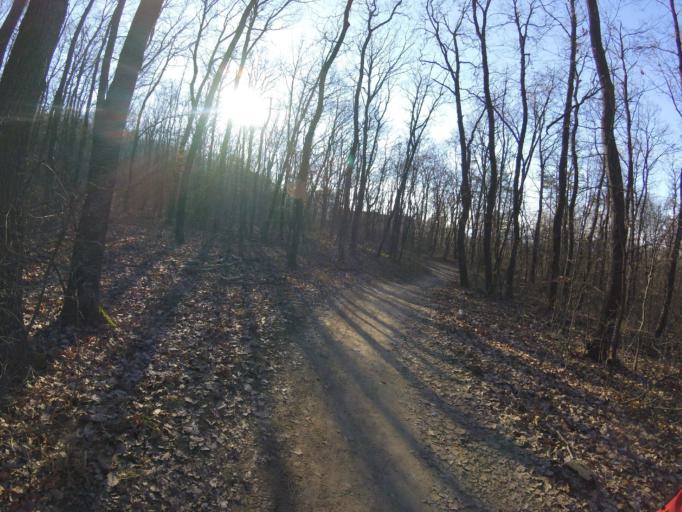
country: HU
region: Pest
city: Budakeszi
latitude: 47.5043
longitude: 18.9446
